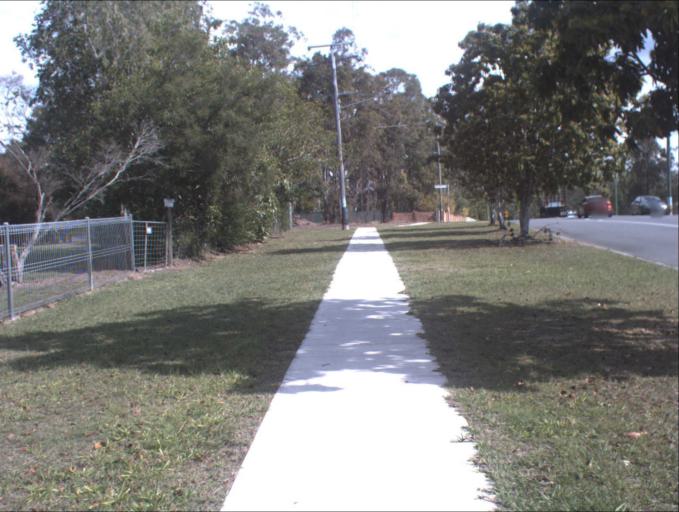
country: AU
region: Queensland
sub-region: Logan
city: Park Ridge South
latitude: -27.7020
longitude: 153.0101
